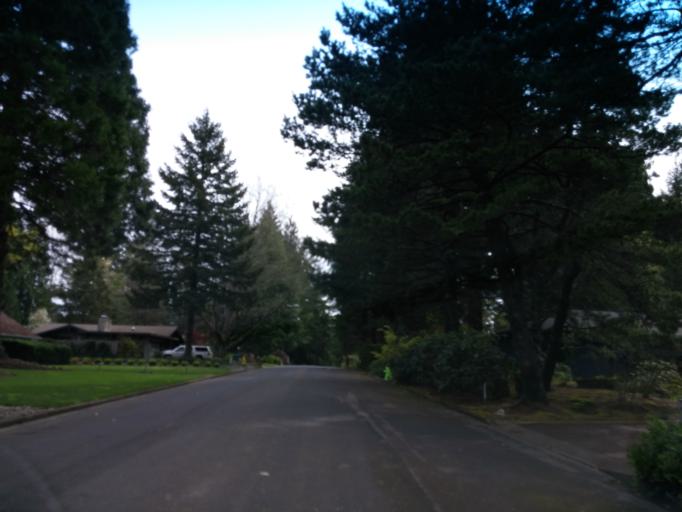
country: US
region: Oregon
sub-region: Washington County
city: Cedar Mill
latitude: 45.5362
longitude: -122.8029
